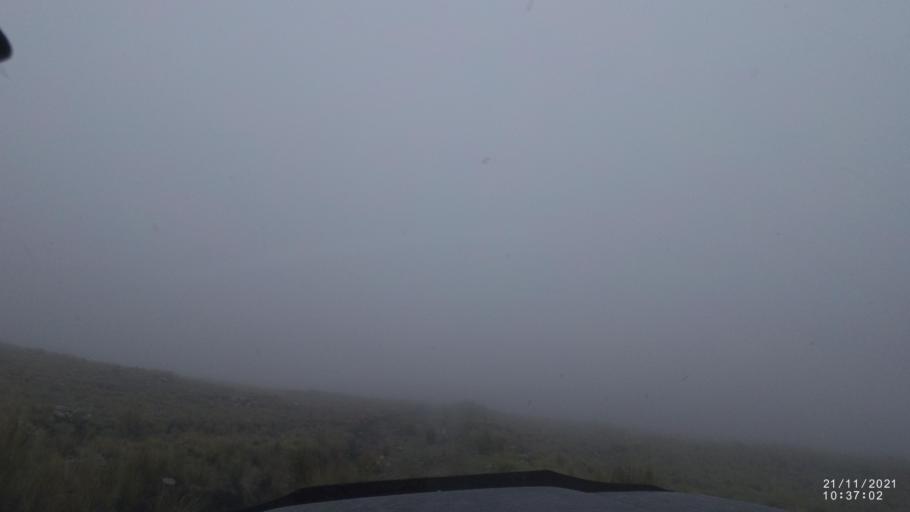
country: BO
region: Cochabamba
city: Cochabamba
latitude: -16.9702
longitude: -66.2682
